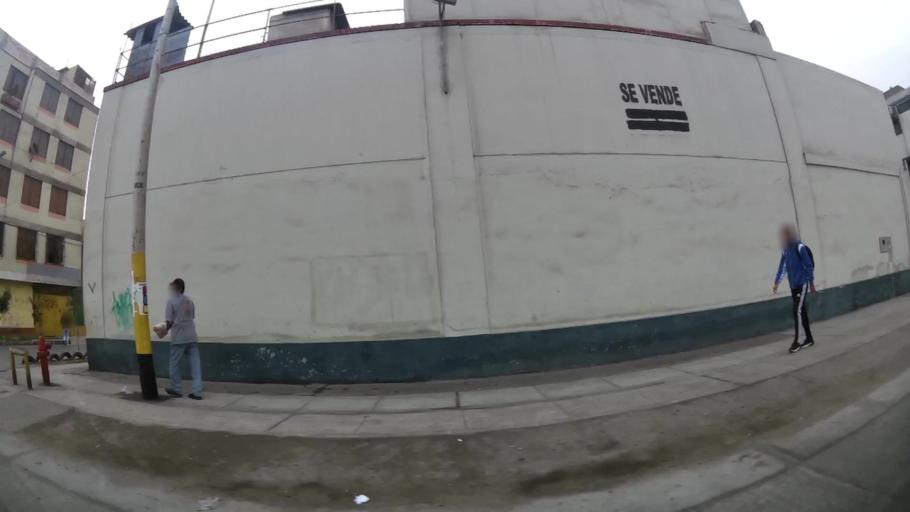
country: PE
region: Lima
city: Lima
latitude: -12.0643
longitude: -77.0534
